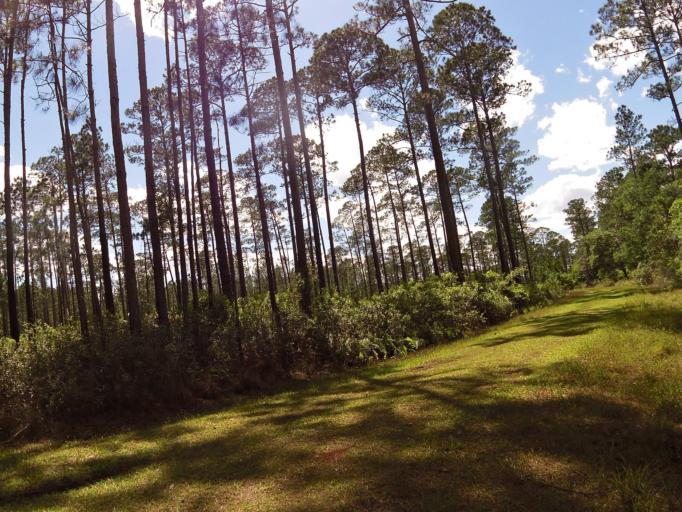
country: US
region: Florida
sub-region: Clay County
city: Green Cove Springs
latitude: 29.9662
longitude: -81.6402
